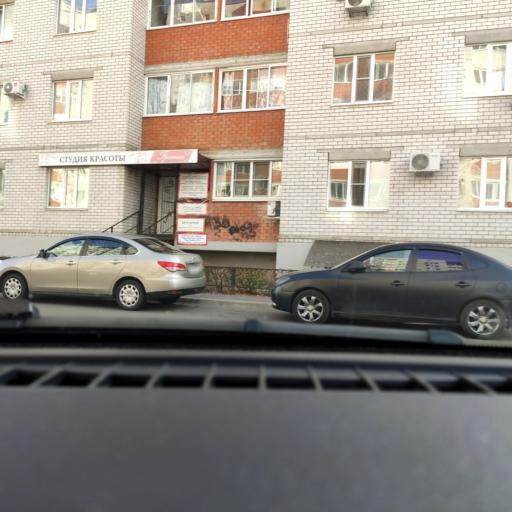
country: RU
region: Voronezj
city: Somovo
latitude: 51.7405
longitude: 39.3118
